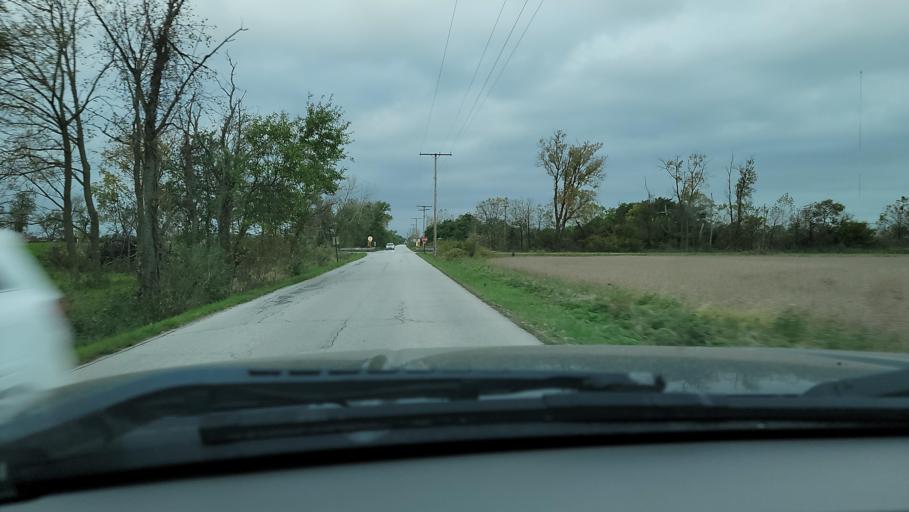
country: US
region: Indiana
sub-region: Porter County
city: South Haven
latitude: 41.5613
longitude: -87.1518
